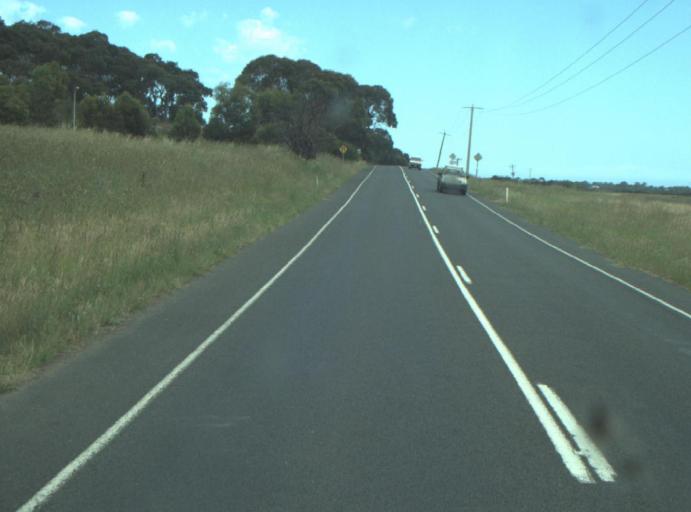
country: AU
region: Victoria
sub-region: Greater Geelong
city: Leopold
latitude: -38.2473
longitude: 144.5047
